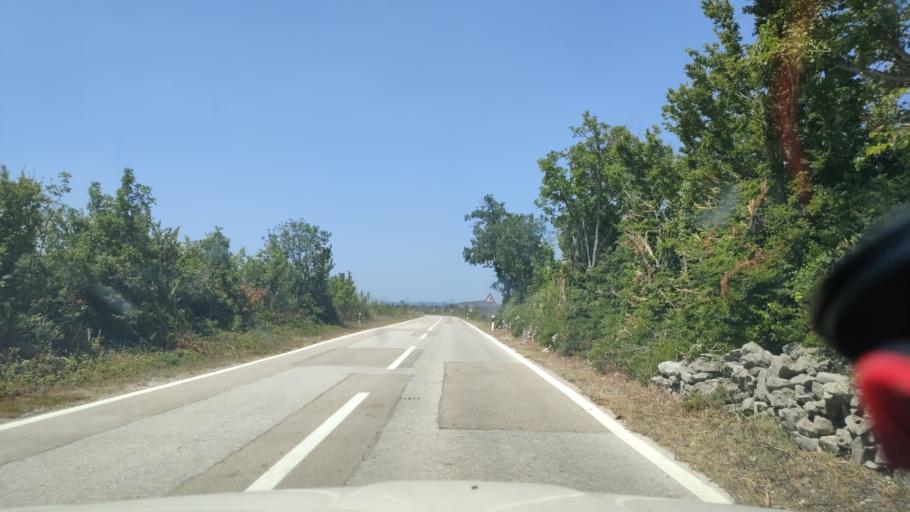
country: HR
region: Sibensko-Kniniska
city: Kistanje
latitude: 43.9770
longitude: 15.9284
